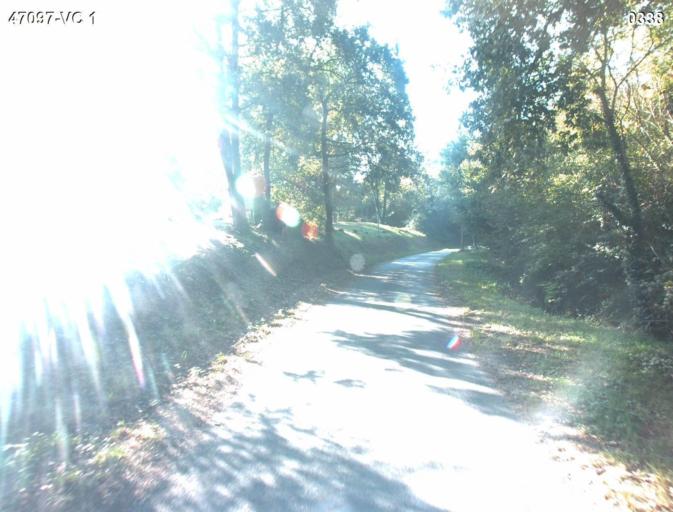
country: FR
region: Aquitaine
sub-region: Departement du Lot-et-Garonne
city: Vianne
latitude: 44.2187
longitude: 0.3488
